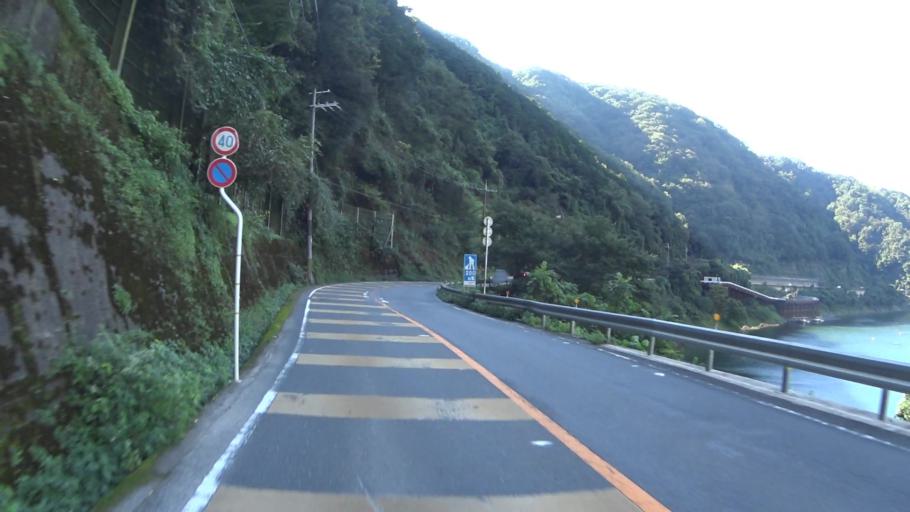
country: JP
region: Kyoto
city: Uji
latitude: 34.8682
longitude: 135.8354
